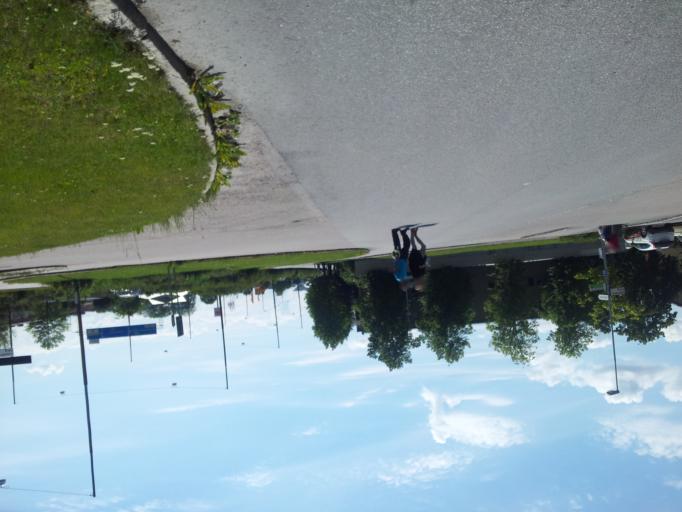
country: SE
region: Uppsala
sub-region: Uppsala Kommun
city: Uppsala
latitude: 59.8705
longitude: 17.6556
